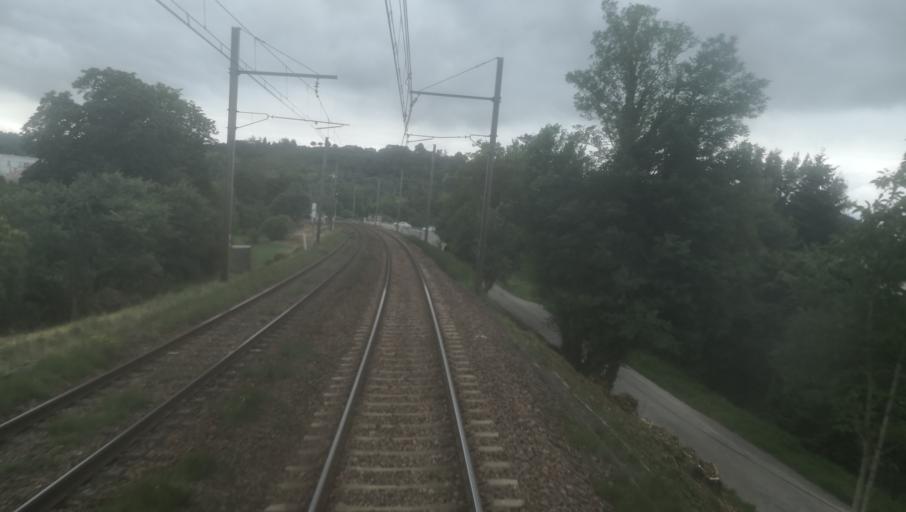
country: FR
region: Midi-Pyrenees
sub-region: Departement du Tarn-et-Garonne
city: Moissac
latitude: 44.1027
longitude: 1.1043
